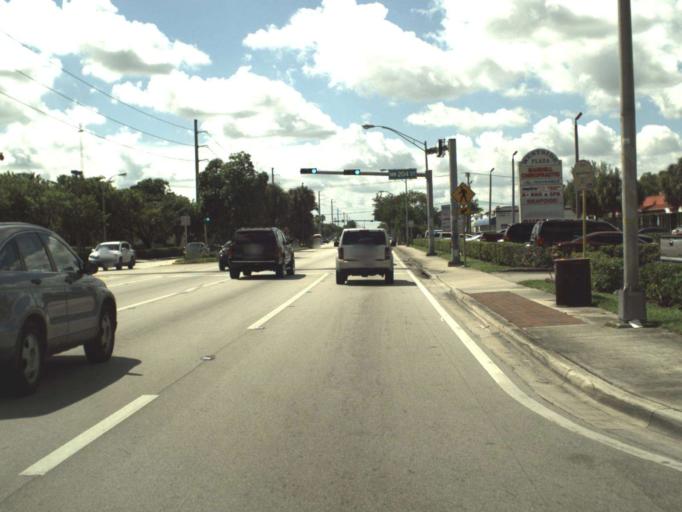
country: US
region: Florida
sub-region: Miami-Dade County
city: Andover
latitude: 25.9634
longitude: -80.2060
